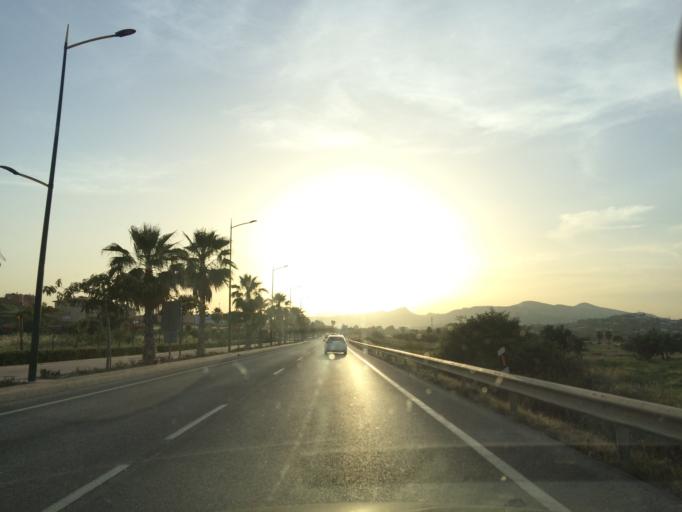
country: ES
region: Andalusia
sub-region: Provincia de Malaga
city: Alhaurin de la Torre
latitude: 36.6692
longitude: -4.5492
